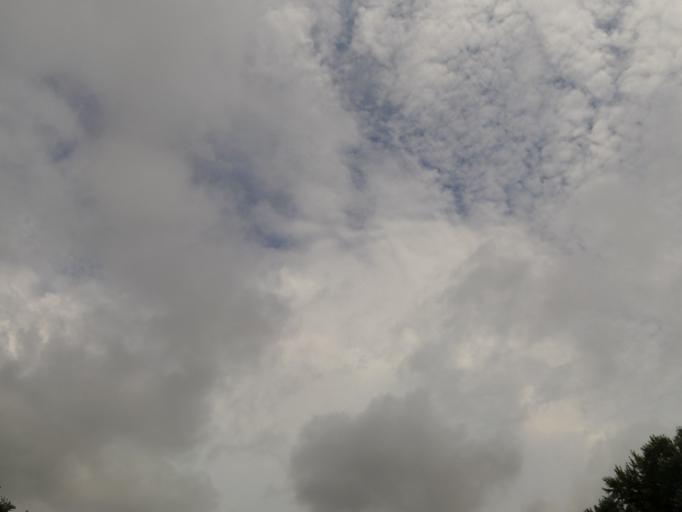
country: US
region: Illinois
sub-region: Jefferson County
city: Ina
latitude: 38.1130
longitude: -88.9117
